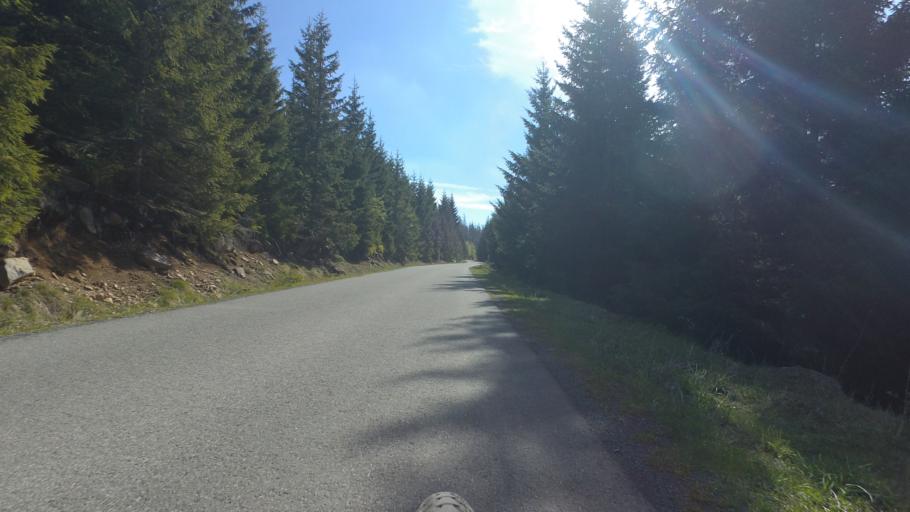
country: DE
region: Lower Saxony
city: Braunlage
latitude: 51.7799
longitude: 10.6351
